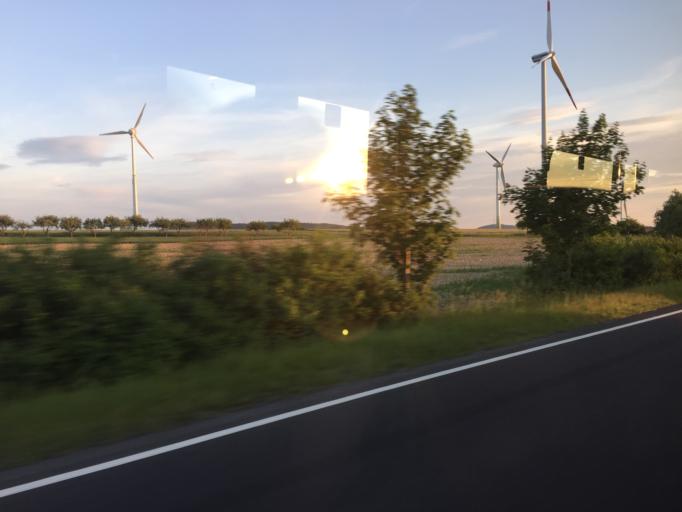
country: DE
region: Saxony
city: Reichenbach
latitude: 51.1484
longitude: 14.7837
